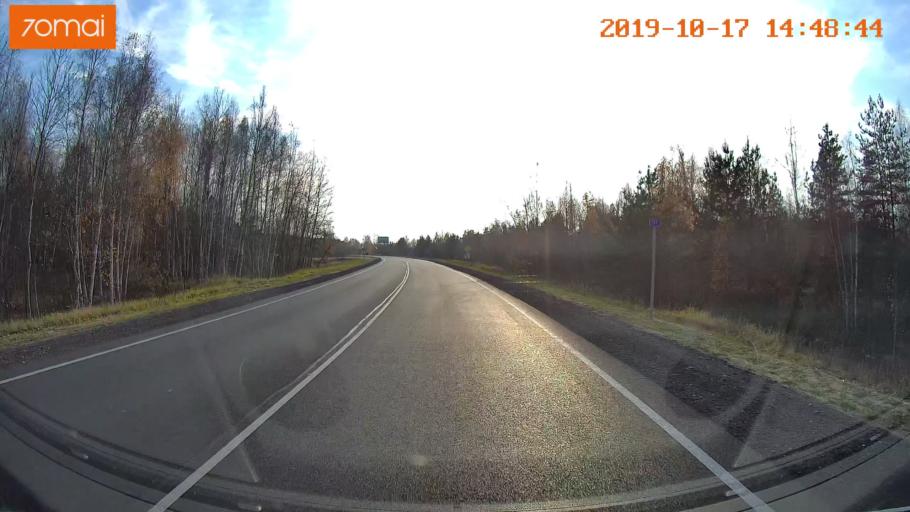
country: RU
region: Rjazan
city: Solotcha
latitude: 54.7559
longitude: 39.8401
